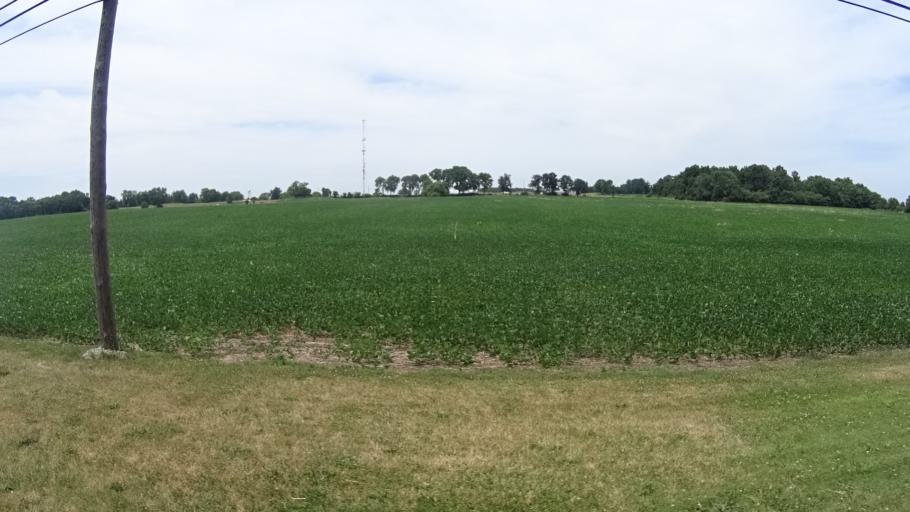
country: US
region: Ohio
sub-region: Erie County
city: Sandusky
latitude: 41.3982
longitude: -82.7821
